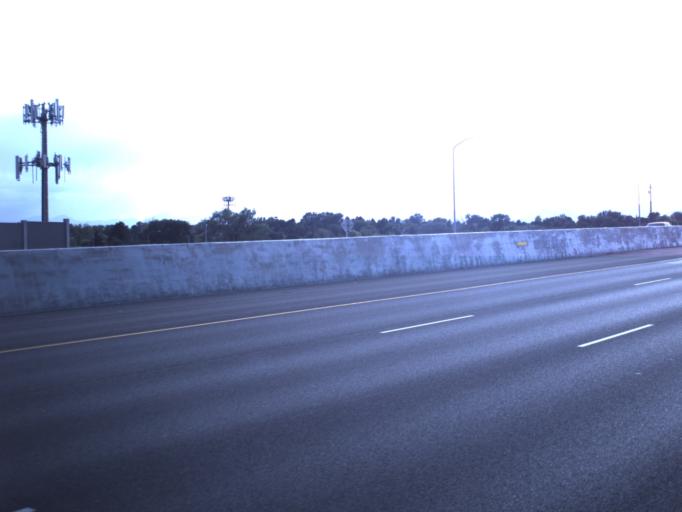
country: US
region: Utah
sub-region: Salt Lake County
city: Taylorsville
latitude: 40.6448
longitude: -111.9367
